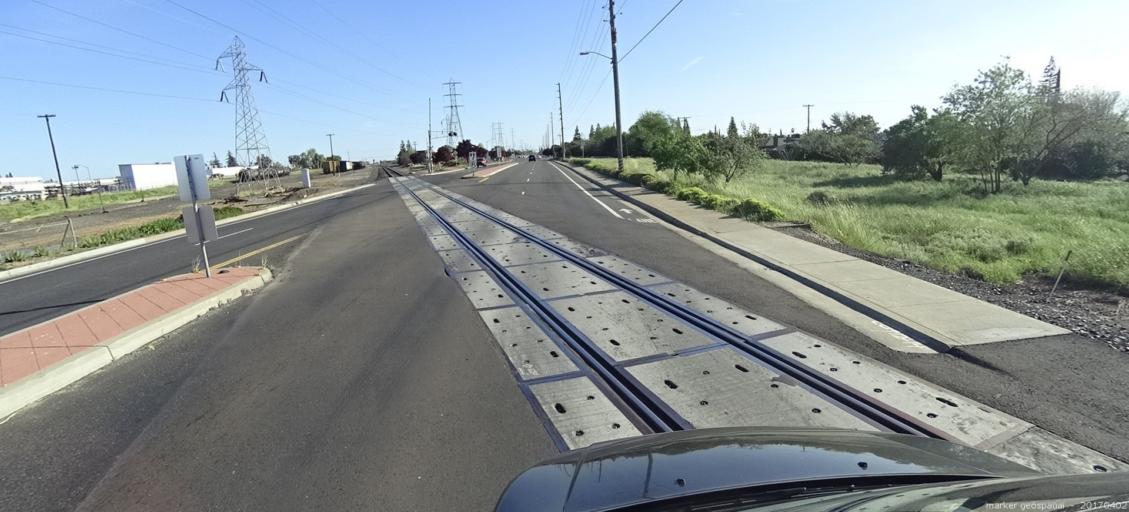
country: US
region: California
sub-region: Sacramento County
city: Florin
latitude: 38.5297
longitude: -121.4093
